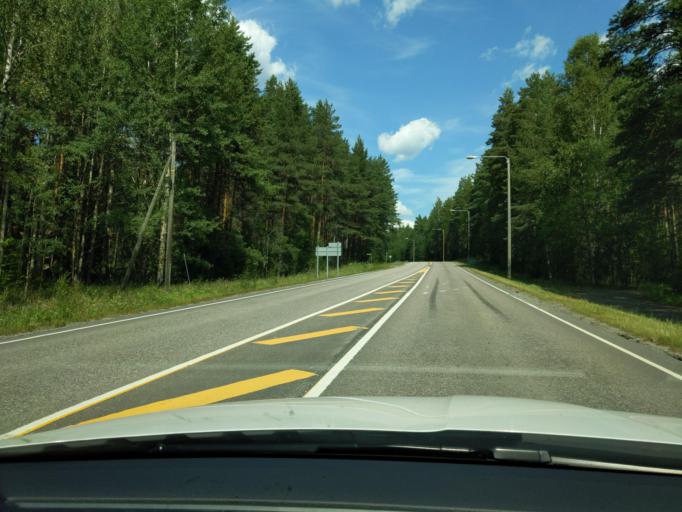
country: FI
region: Paijanne Tavastia
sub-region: Lahti
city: Heinola
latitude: 61.2502
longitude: 26.0609
